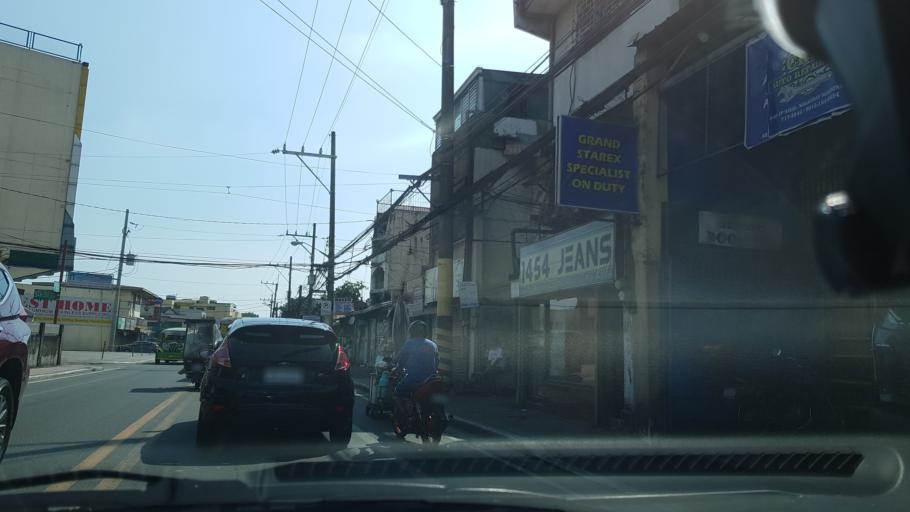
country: PH
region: Metro Manila
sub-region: Marikina
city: Calumpang
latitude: 14.6439
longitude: 121.0956
